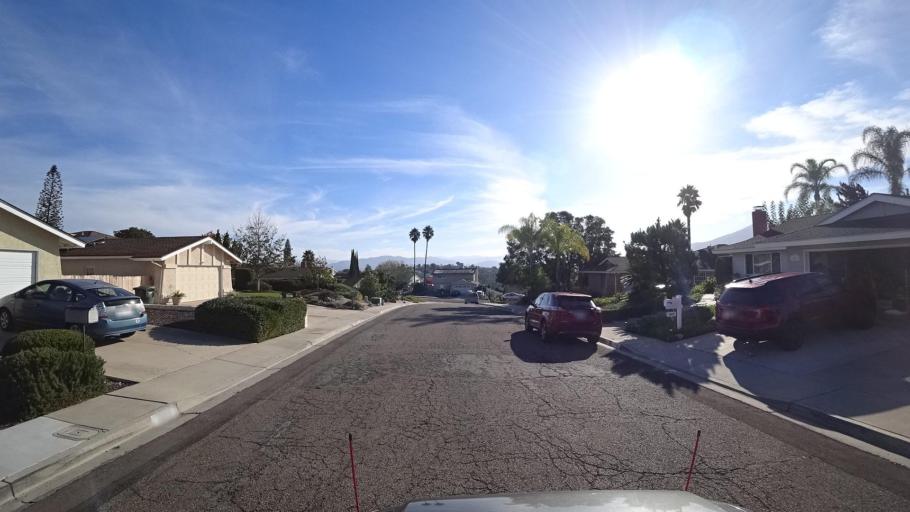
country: US
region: California
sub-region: San Diego County
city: Spring Valley
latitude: 32.7374
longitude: -116.9778
